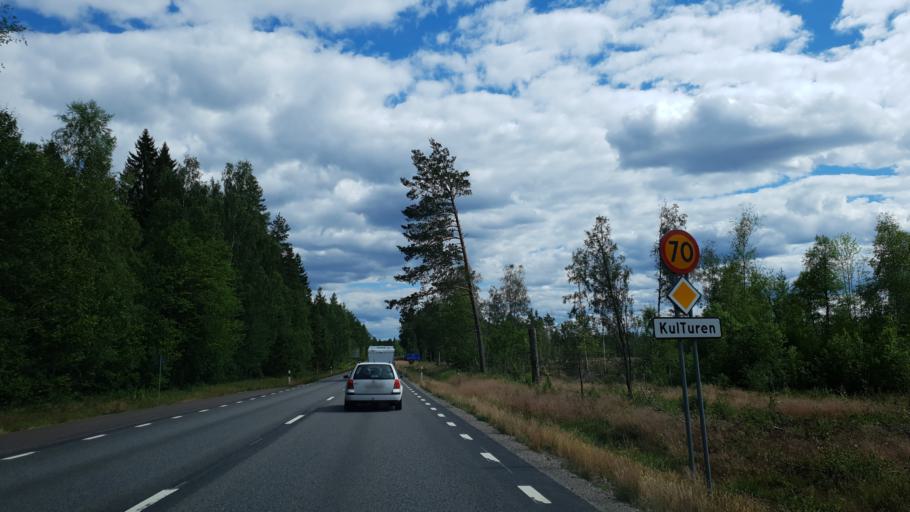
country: SE
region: Kronoberg
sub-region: Lessebo Kommun
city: Lessebo
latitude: 56.8308
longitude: 15.3973
